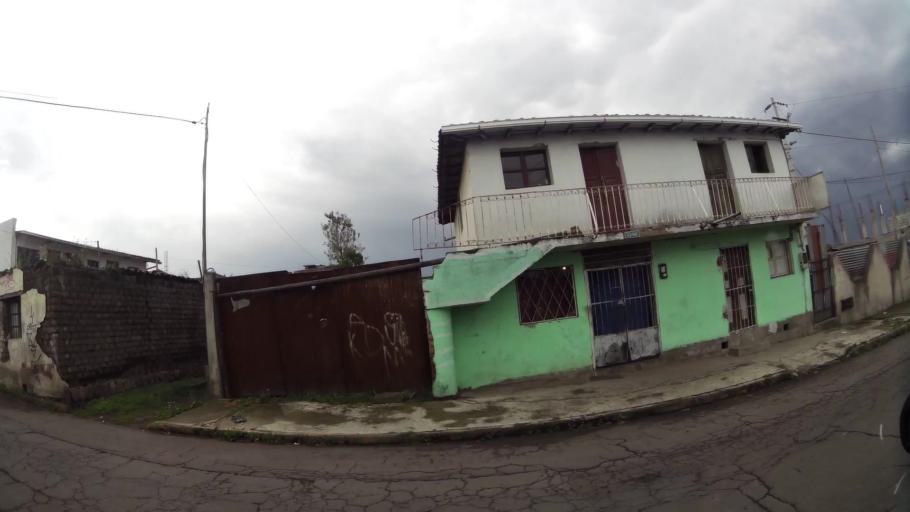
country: EC
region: Pichincha
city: Sangolqui
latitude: -0.3520
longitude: -78.5568
